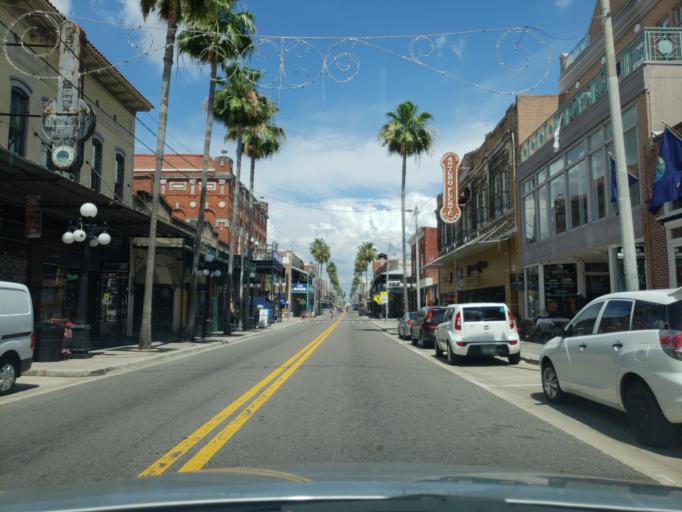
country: US
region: Florida
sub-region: Hillsborough County
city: Tampa
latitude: 27.9603
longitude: -82.4426
